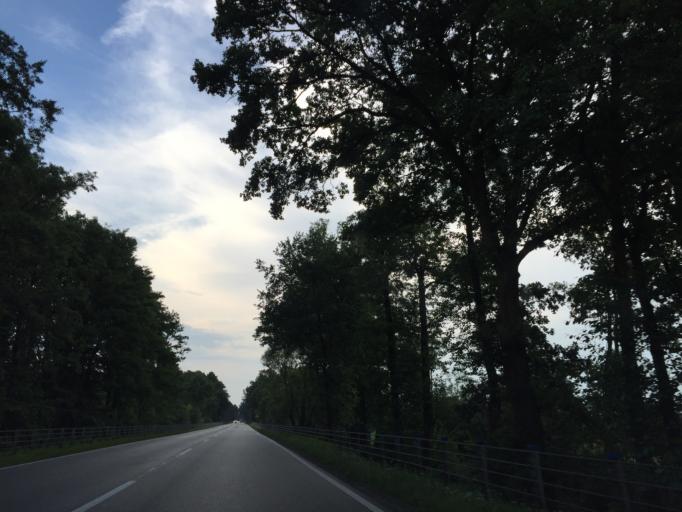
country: PL
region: Masovian Voivodeship
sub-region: Powiat wegrowski
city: Sadowne
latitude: 52.6508
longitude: 21.8467
